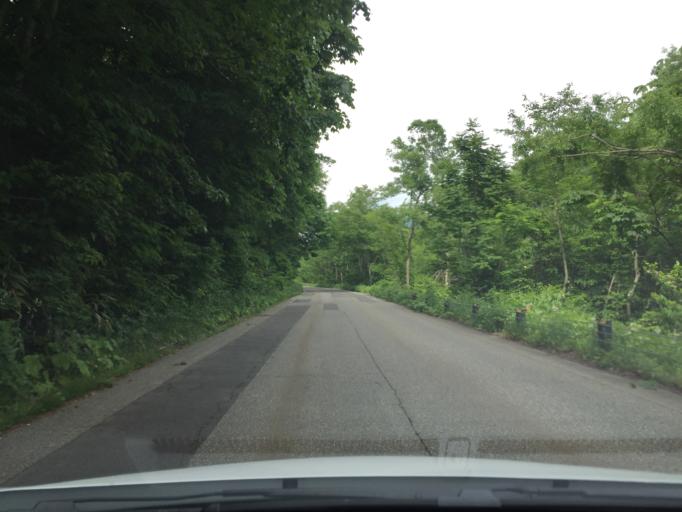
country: JP
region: Fukushima
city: Inawashiro
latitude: 37.6487
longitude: 140.0368
